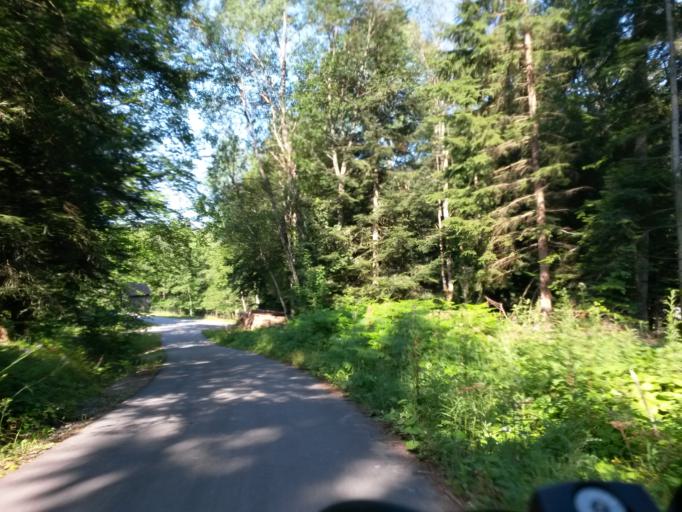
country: DE
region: Baden-Wuerttemberg
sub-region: Karlsruhe Region
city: Bad Wildbad
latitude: 48.7024
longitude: 8.5344
